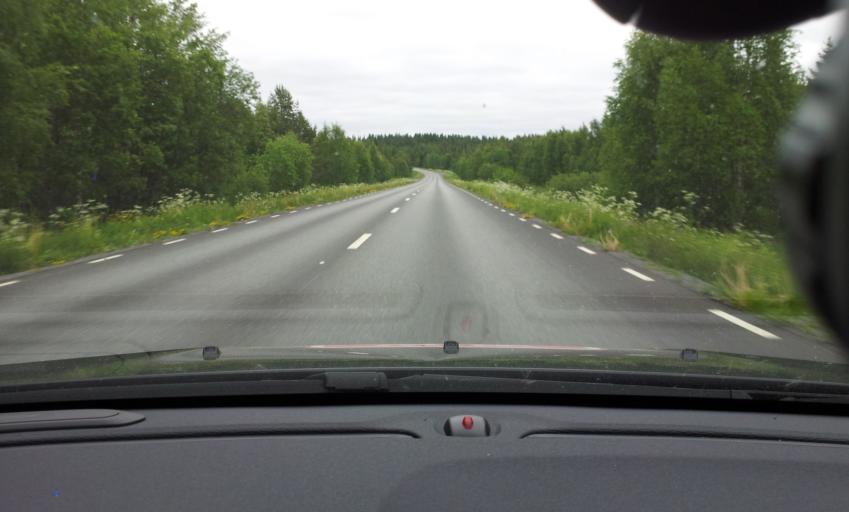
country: SE
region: Jaemtland
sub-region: Krokoms Kommun
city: Krokom
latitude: 63.0893
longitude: 14.2989
